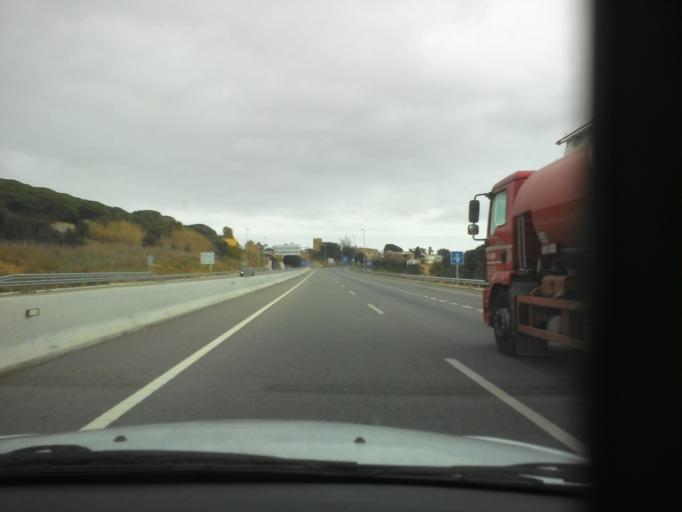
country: ES
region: Catalonia
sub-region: Provincia de Girona
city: Castell-Platja d'Aro
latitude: 41.8212
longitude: 3.0555
